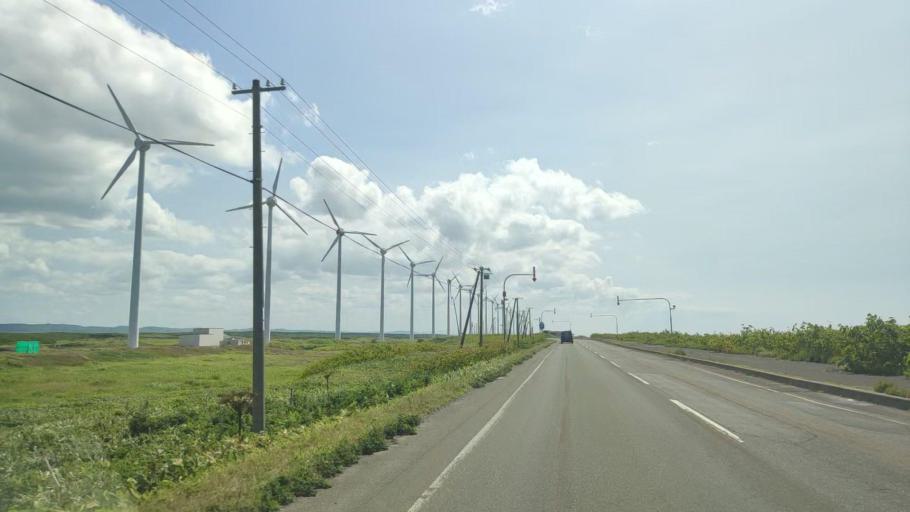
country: JP
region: Hokkaido
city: Makubetsu
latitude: 44.9783
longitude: 141.6947
